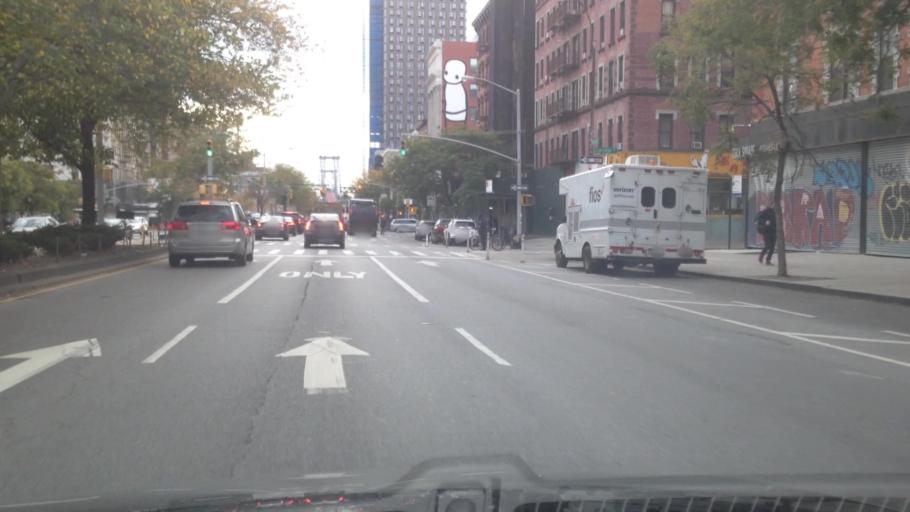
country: US
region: New York
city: New York City
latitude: 40.7196
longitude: -73.9918
